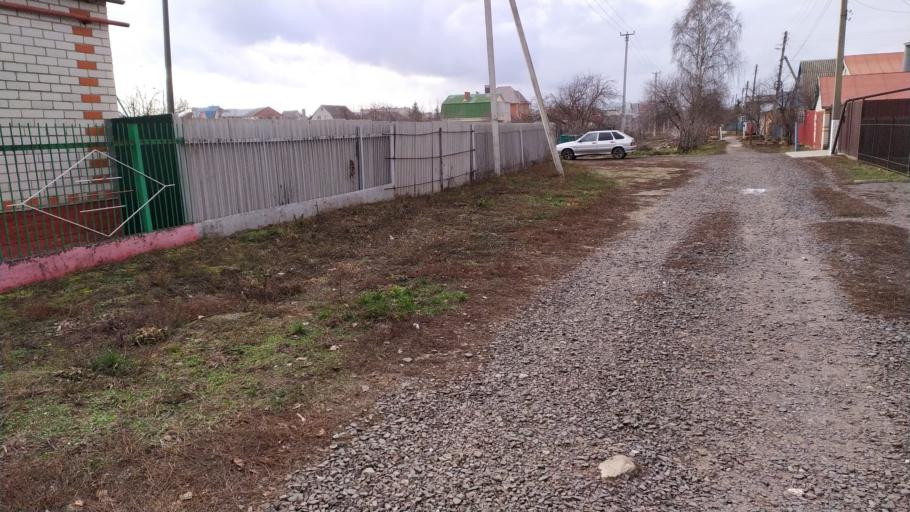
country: RU
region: Kursk
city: Kursk
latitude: 51.6409
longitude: 36.1470
